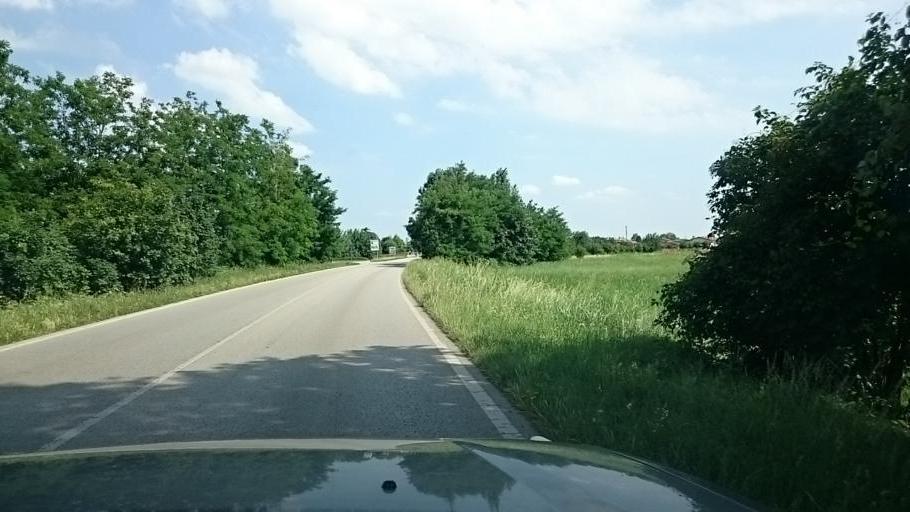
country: IT
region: Veneto
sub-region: Provincia di Vicenza
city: Cartigliano
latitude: 45.7207
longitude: 11.7020
